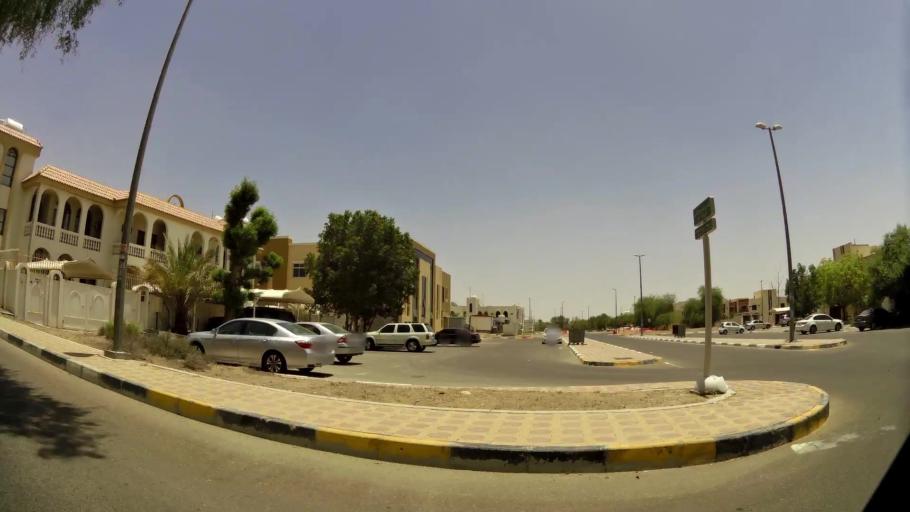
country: OM
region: Al Buraimi
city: Al Buraymi
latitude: 24.2619
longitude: 55.7272
